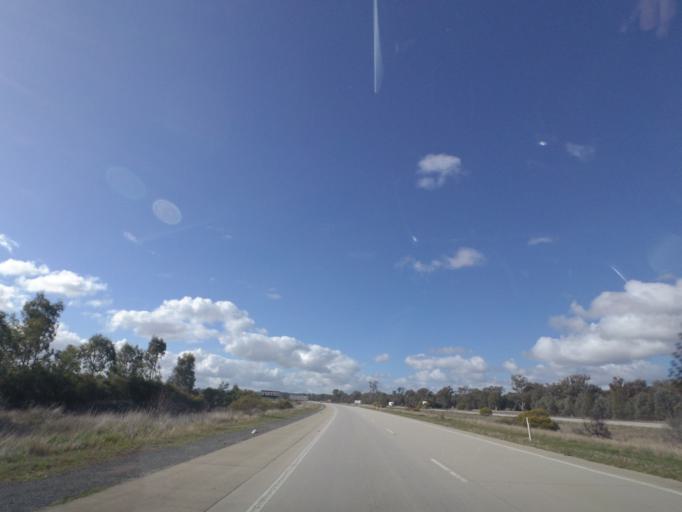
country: AU
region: New South Wales
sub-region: Greater Hume Shire
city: Holbrook
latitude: -35.9133
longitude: 147.1509
